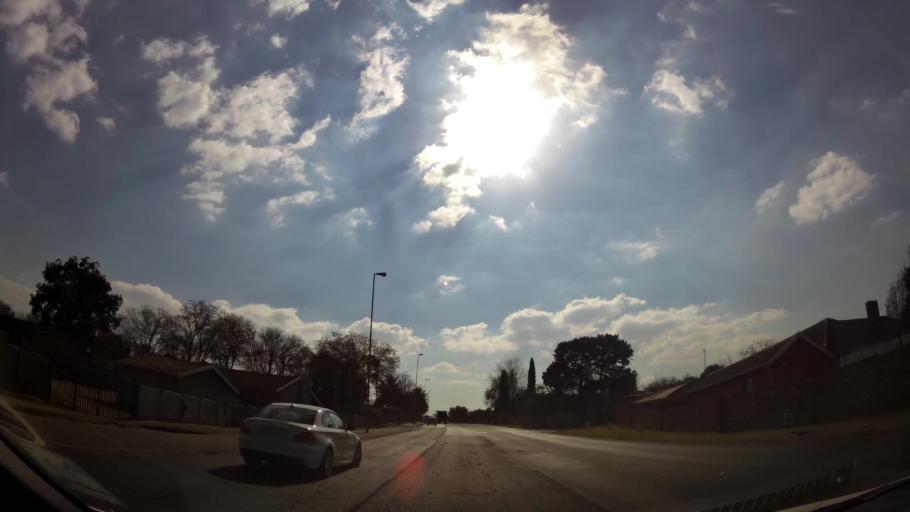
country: ZA
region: Gauteng
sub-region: Ekurhuleni Metropolitan Municipality
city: Boksburg
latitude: -26.1900
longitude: 28.2168
